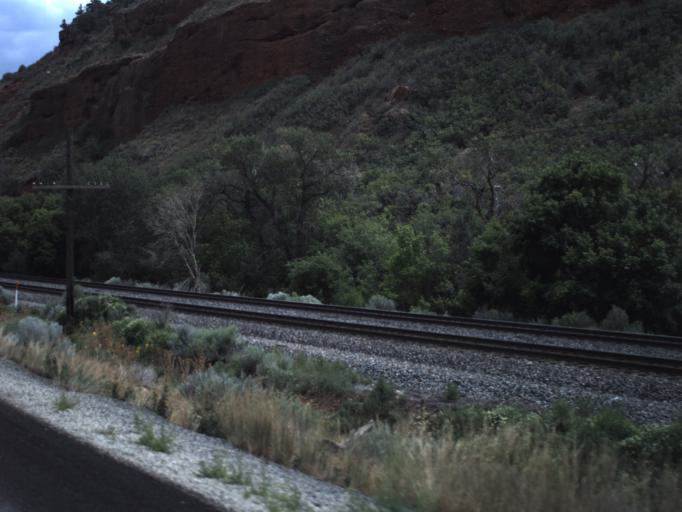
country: US
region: Utah
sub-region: Utah County
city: Mapleton
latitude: 39.9913
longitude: -111.3836
